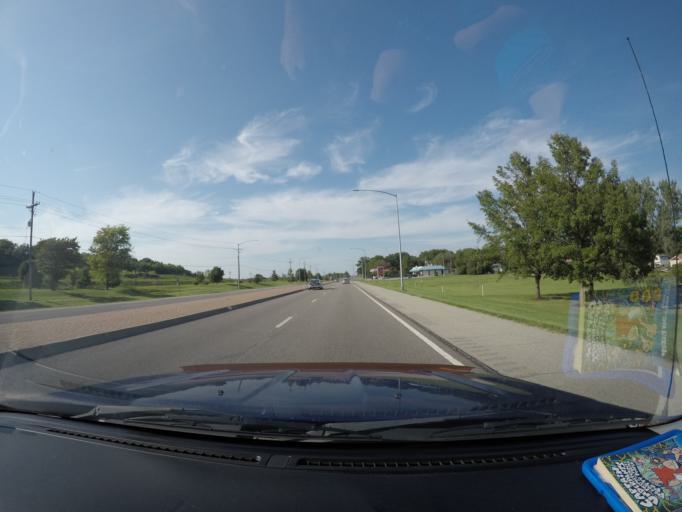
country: US
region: Kansas
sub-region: Leavenworth County
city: Lansing
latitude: 39.2396
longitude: -94.9001
